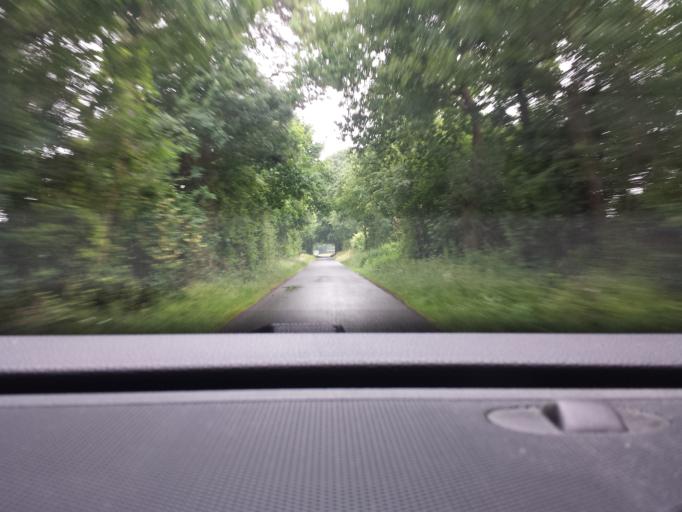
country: DE
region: North Rhine-Westphalia
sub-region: Regierungsbezirk Munster
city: Ahaus
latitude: 52.0666
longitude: 7.0519
